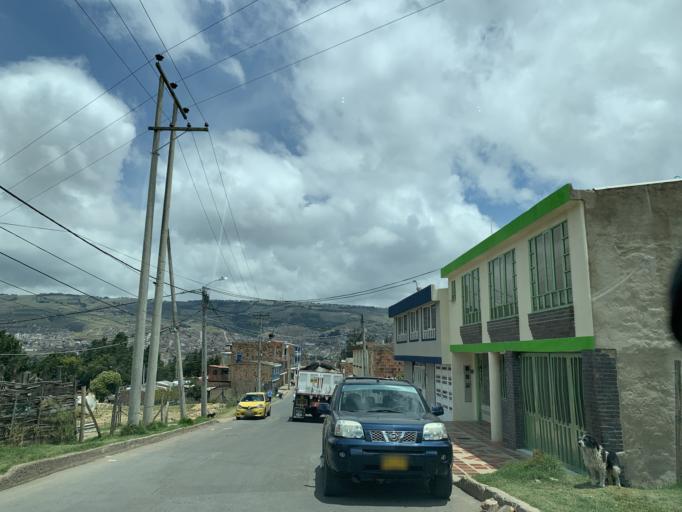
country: CO
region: Boyaca
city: Tunja
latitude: 5.5182
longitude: -73.3526
